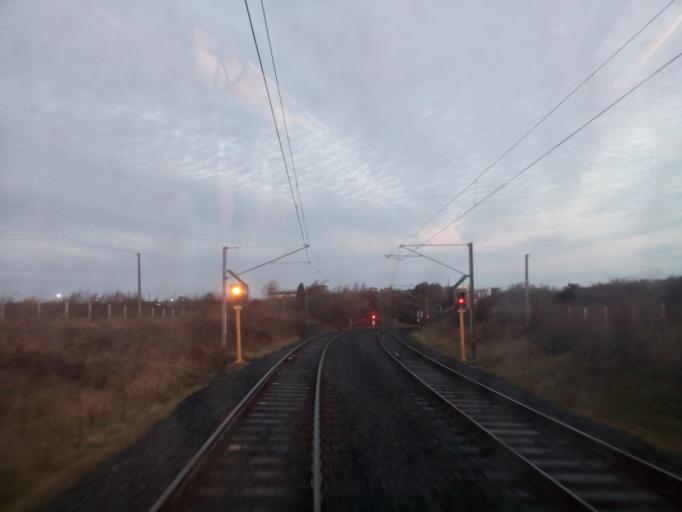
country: GB
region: England
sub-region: Northumberland
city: Ponteland
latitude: 55.0331
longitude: -1.7096
